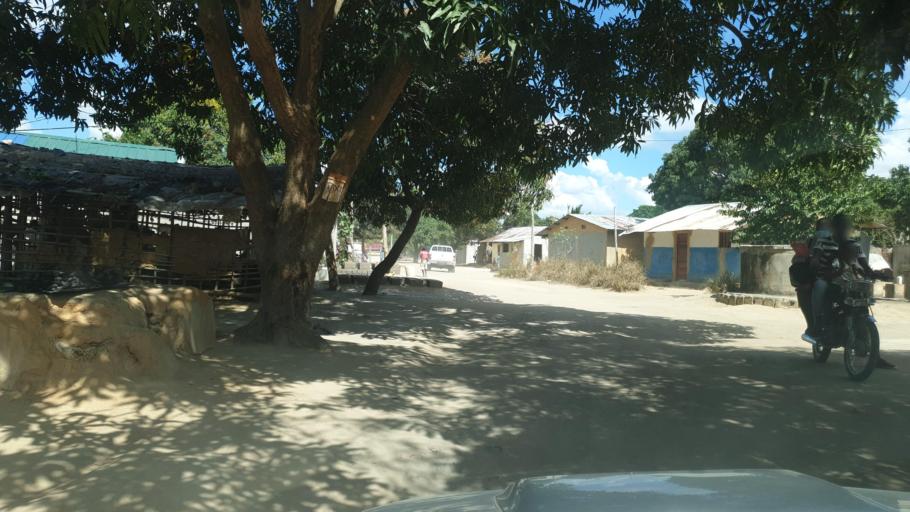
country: MZ
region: Nampula
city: Nacala
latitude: -14.5701
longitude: 40.6990
